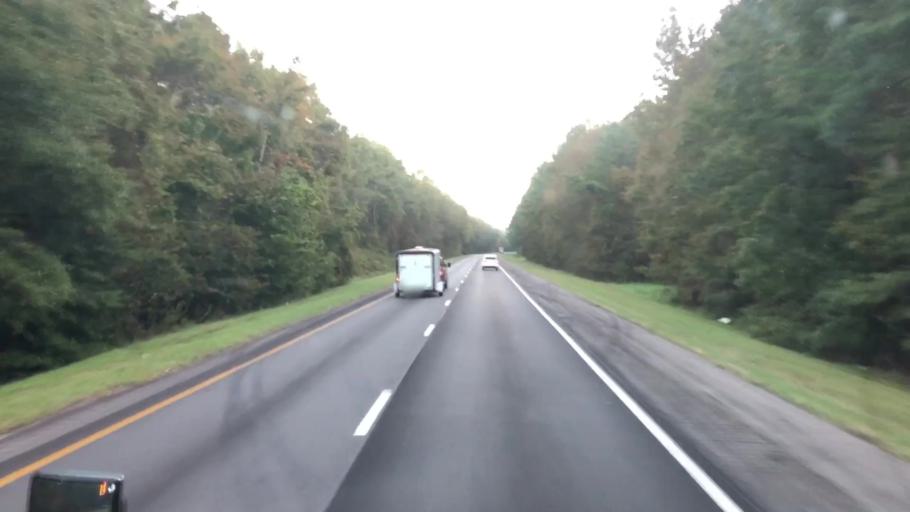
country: US
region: South Carolina
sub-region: Orangeburg County
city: Holly Hill
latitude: 33.5471
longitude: -80.4098
